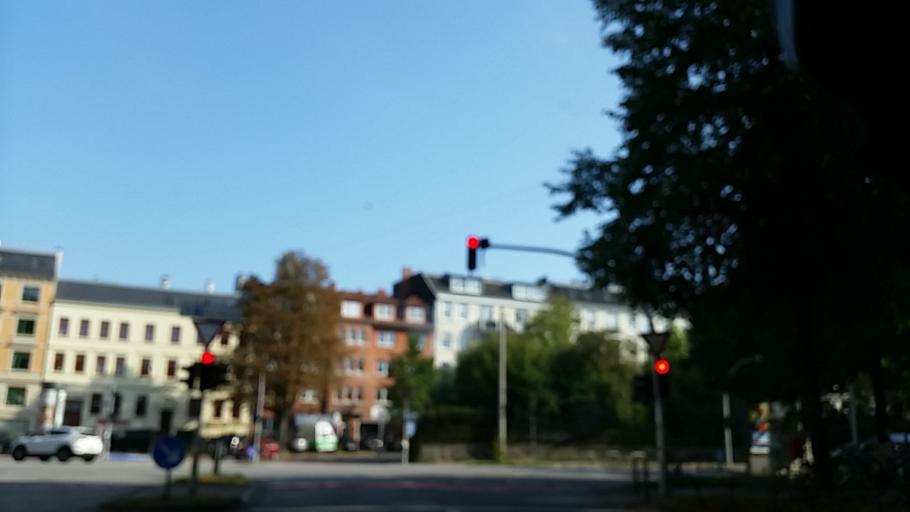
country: DE
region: Hamburg
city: Winterhude
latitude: 53.5923
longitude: 10.0021
